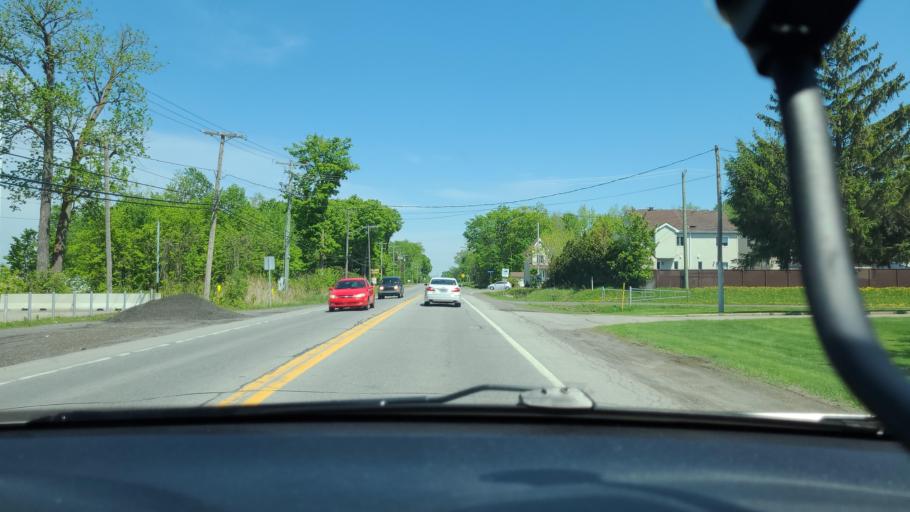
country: CA
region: Quebec
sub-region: Laurentides
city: Saint-Eustache
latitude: 45.5859
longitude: -73.9397
